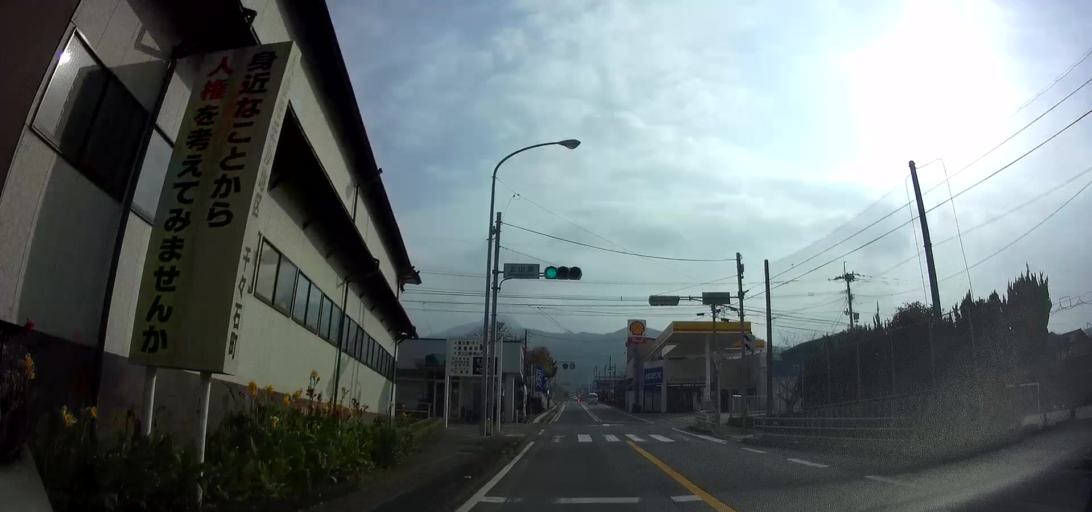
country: JP
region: Nagasaki
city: Shimabara
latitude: 32.7851
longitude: 130.2008
